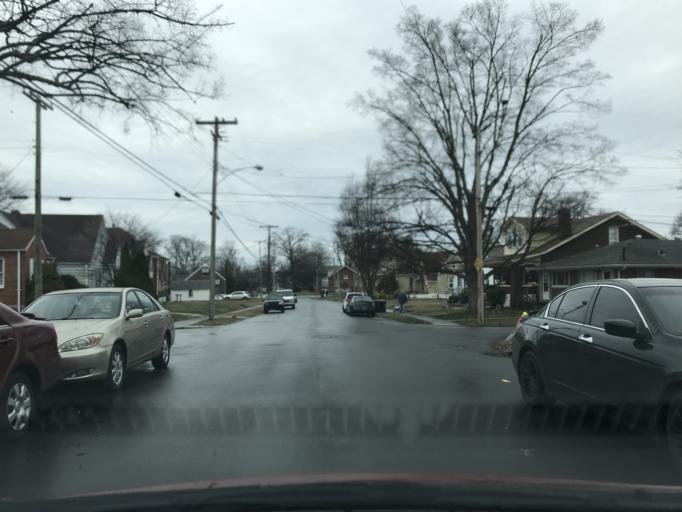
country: US
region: Kentucky
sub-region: Jefferson County
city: Audubon Park
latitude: 38.1766
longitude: -85.7631
